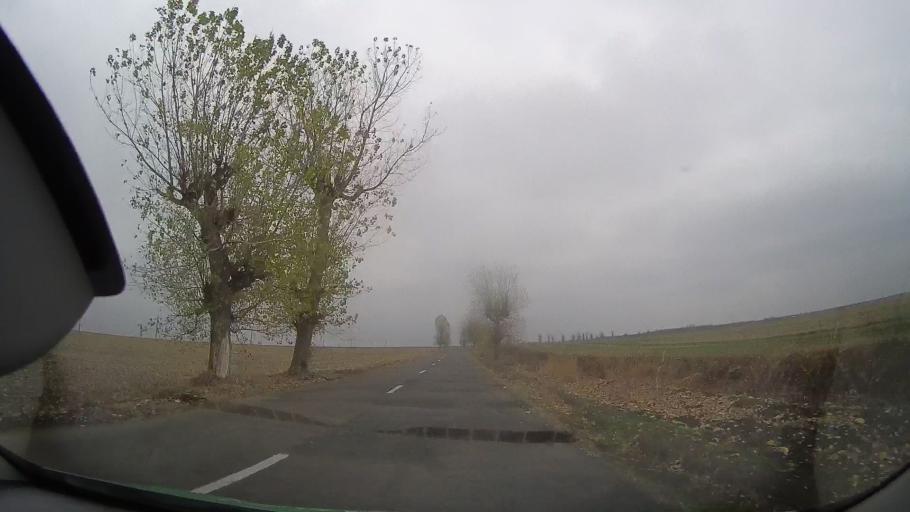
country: RO
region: Ialomita
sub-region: Comuna Grindu
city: Grindu
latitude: 44.7947
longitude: 26.8921
